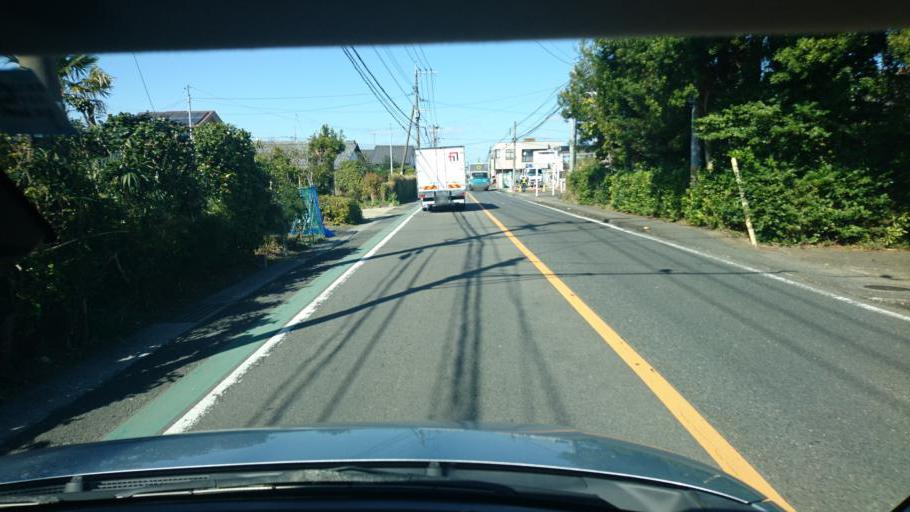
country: JP
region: Miyazaki
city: Miyazaki-shi
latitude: 31.8642
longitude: 131.4322
